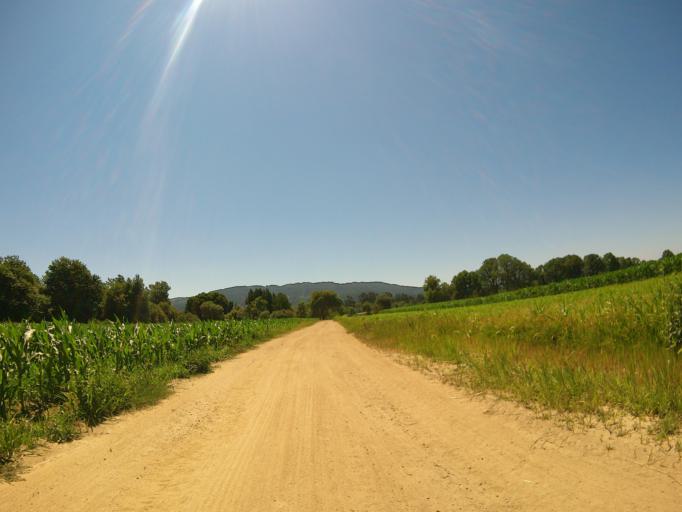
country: PT
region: Viana do Castelo
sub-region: Viana do Castelo
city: Darque
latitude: 41.7192
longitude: -8.7047
